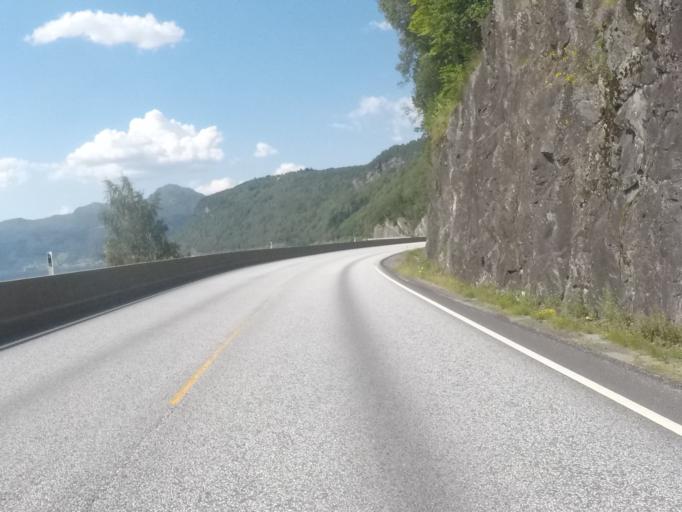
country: NO
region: Sogn og Fjordane
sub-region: Naustdal
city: Naustdal
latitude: 61.4993
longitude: 5.7737
